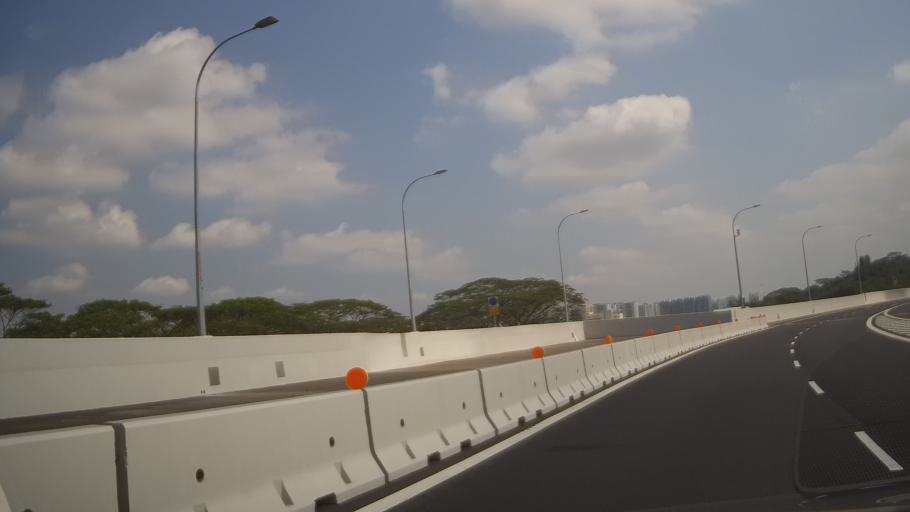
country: MY
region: Johor
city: Kampung Pasir Gudang Baru
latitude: 1.3820
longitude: 103.9147
